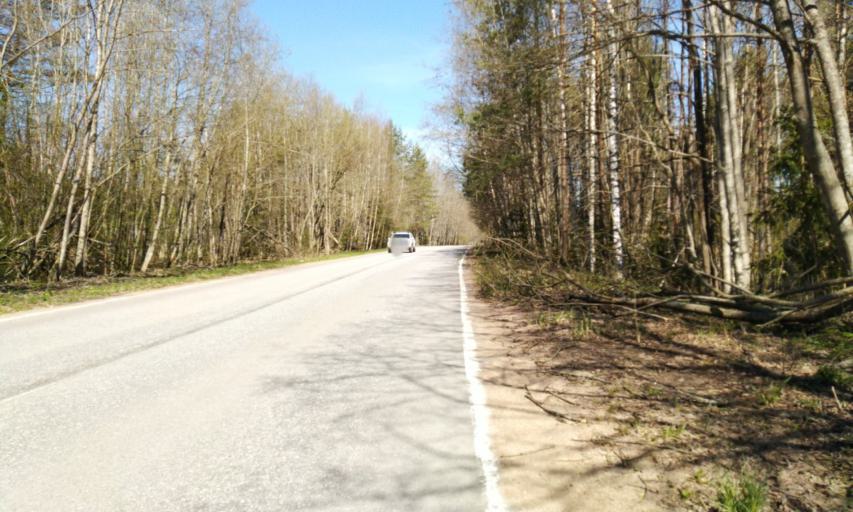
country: RU
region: Leningrad
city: Garbolovo
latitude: 60.4085
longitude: 30.4621
